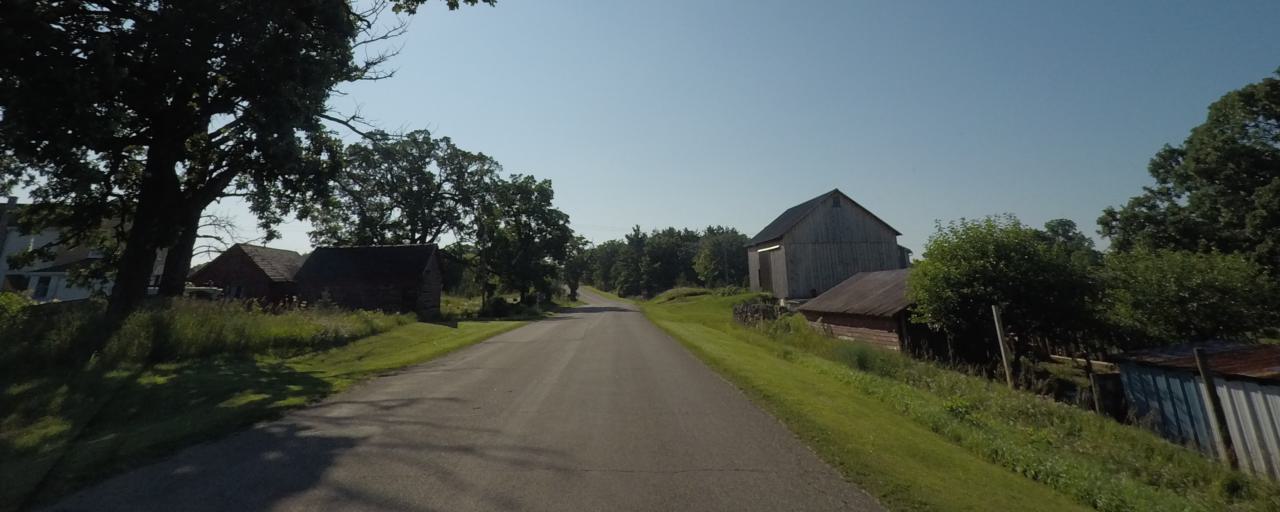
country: US
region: Wisconsin
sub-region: Jefferson County
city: Palmyra
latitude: 42.9181
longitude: -88.5436
